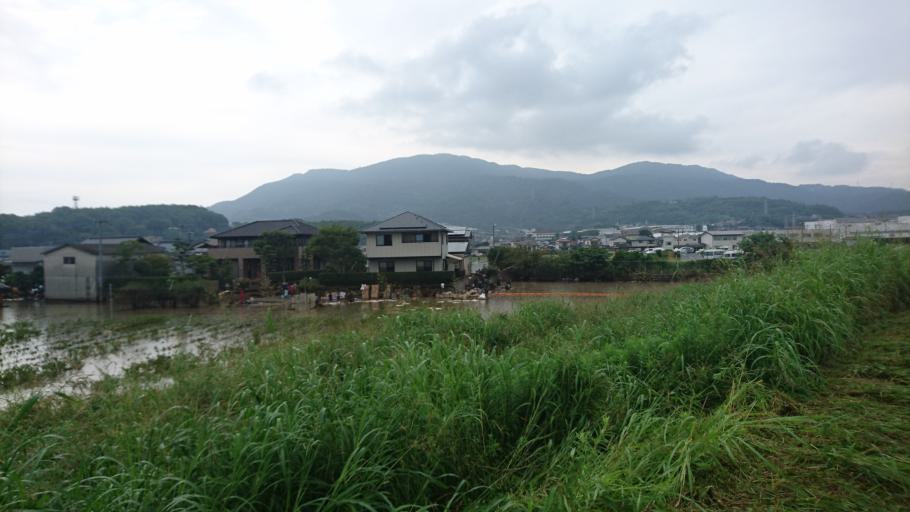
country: JP
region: Saga Prefecture
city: Takeocho-takeo
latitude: 33.2093
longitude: 130.1062
